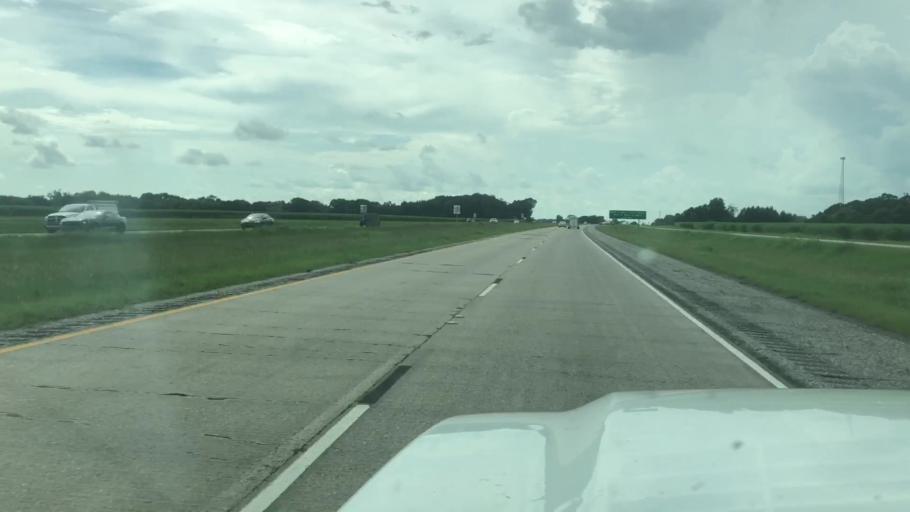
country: US
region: Louisiana
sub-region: Iberia Parish
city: Jeanerette
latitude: 29.8604
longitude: -91.6201
